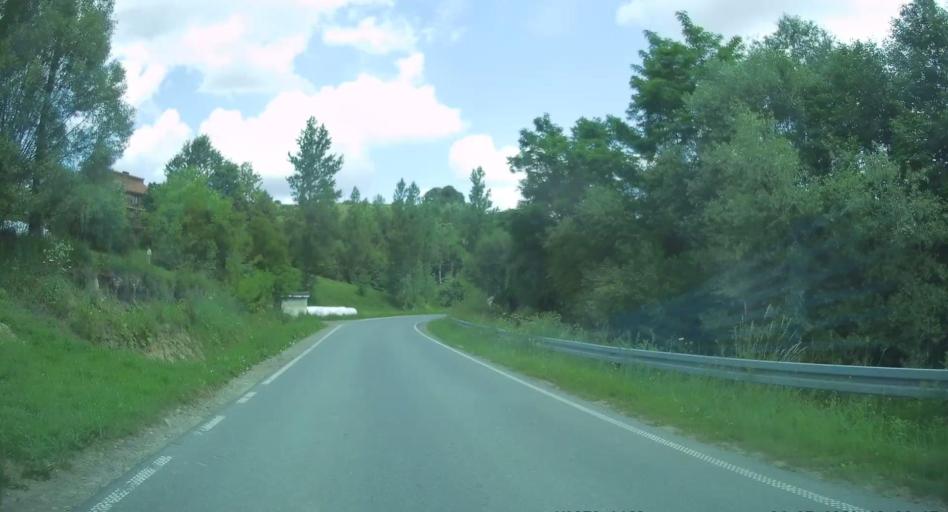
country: PL
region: Lesser Poland Voivodeship
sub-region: Powiat nowosadecki
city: Korzenna
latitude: 49.7276
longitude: 20.7726
